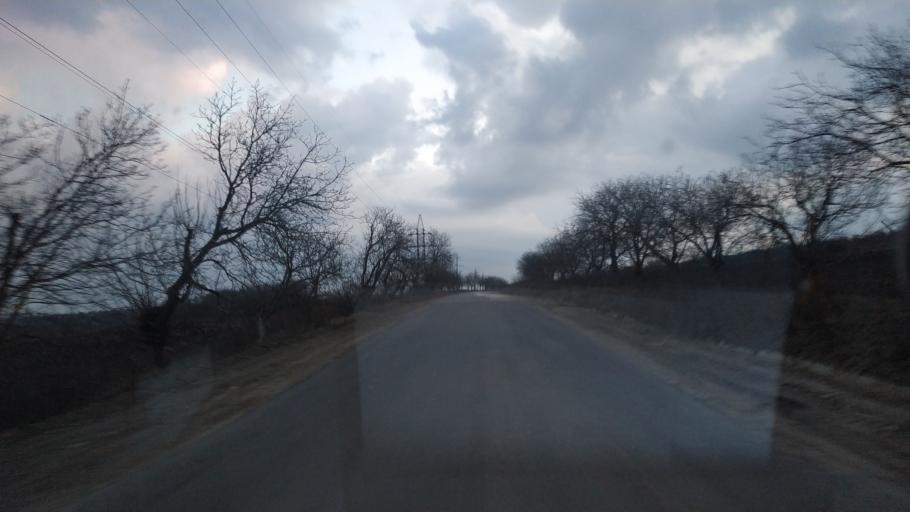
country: MD
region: Anenii Noi
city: Anenii Noi
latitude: 46.9722
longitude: 29.2852
